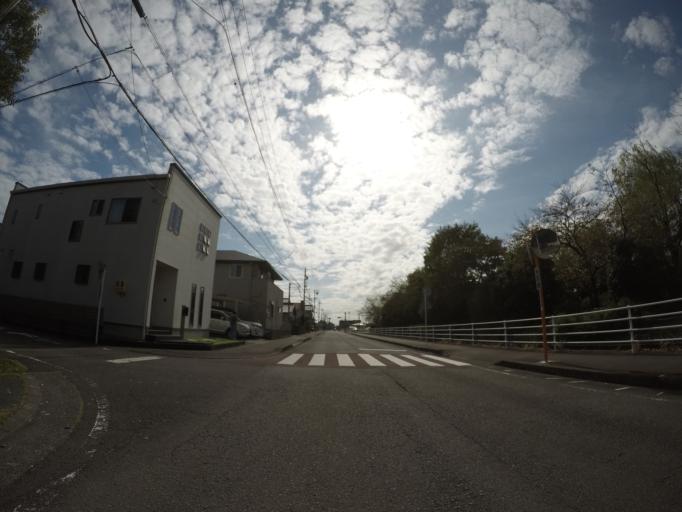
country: JP
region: Shizuoka
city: Yaizu
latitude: 34.8893
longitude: 138.3219
